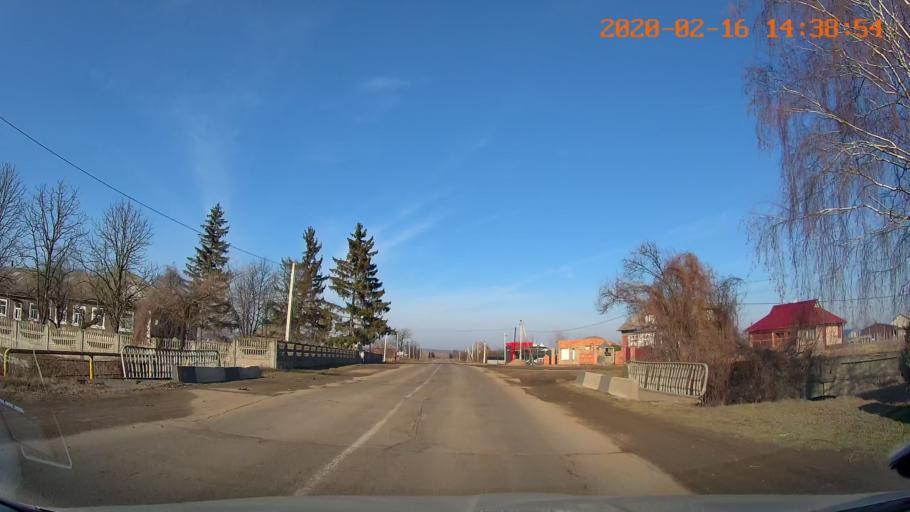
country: RO
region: Botosani
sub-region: Comuna Darabani
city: Bajura
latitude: 48.2361
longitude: 26.5464
